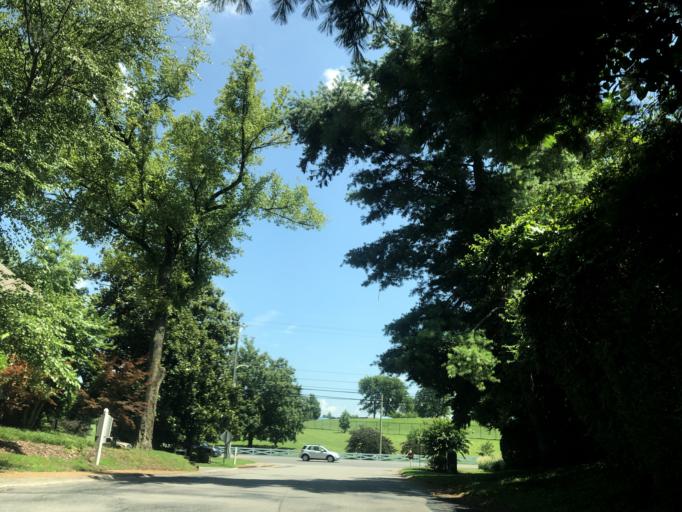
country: US
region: Tennessee
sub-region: Davidson County
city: Lakewood
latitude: 36.1711
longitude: -86.6540
